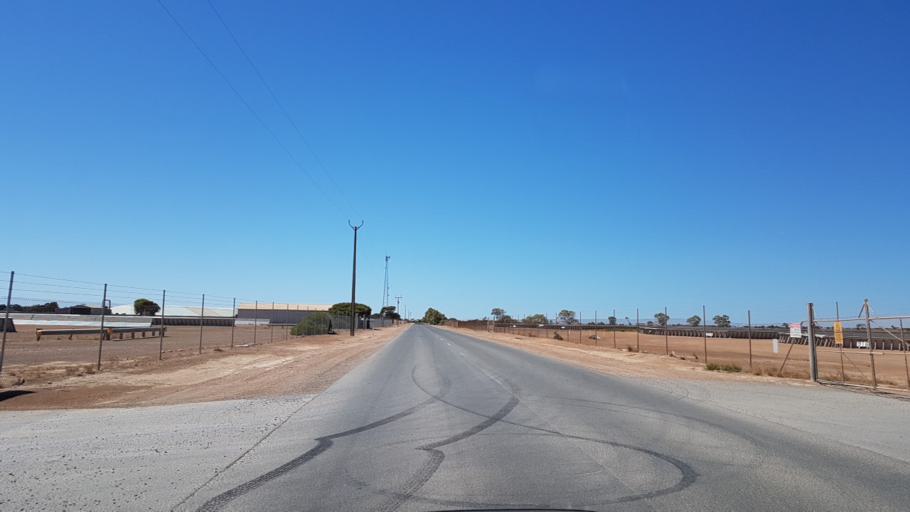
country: AU
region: South Australia
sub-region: Copper Coast
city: Wallaroo
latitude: -33.9387
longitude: 137.6110
